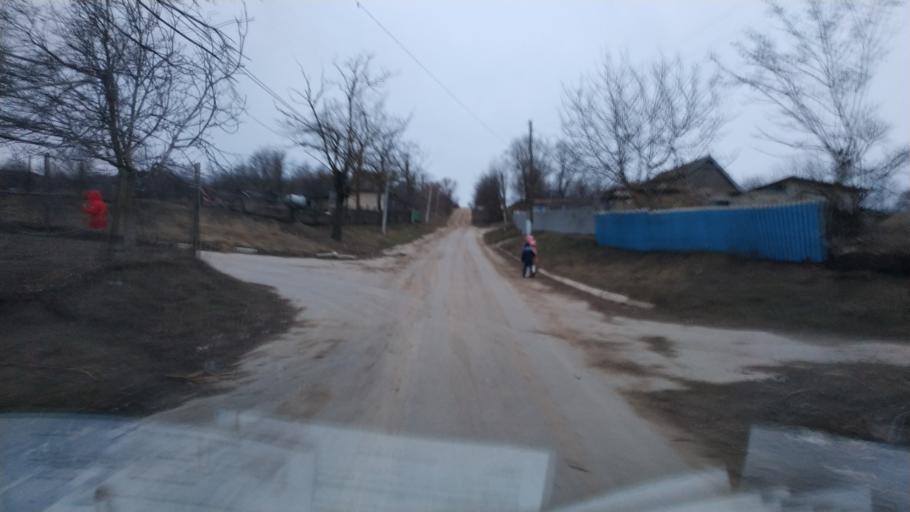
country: MD
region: Causeni
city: Causeni
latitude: 46.4970
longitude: 29.4022
